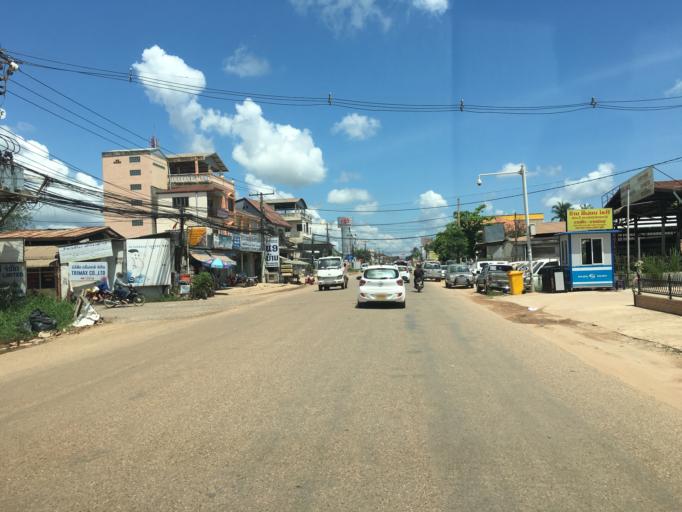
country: TH
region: Nong Khai
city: Si Chiang Mai
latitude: 17.9823
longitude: 102.5536
